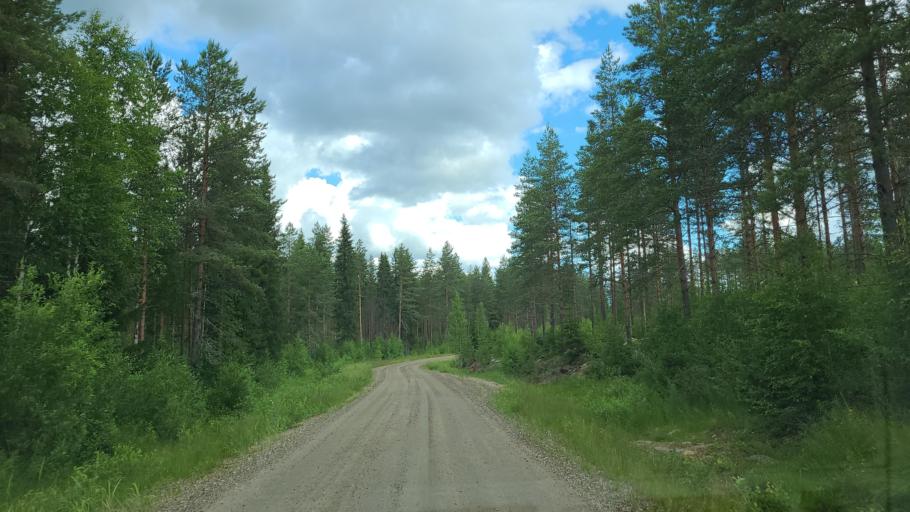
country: FI
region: Northern Savo
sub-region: Koillis-Savo
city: Kaavi
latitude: 63.0329
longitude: 28.7838
